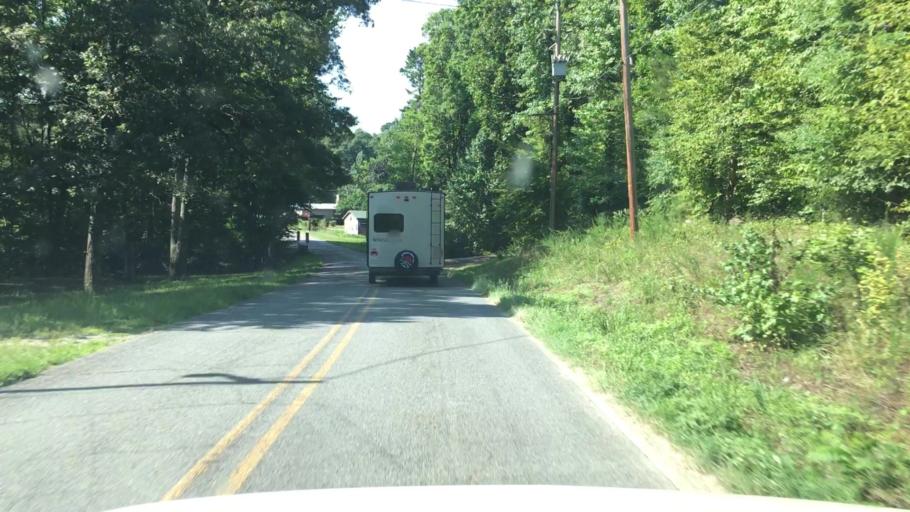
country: US
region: Arkansas
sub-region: Garland County
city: Rockwell
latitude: 34.5238
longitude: -93.3362
